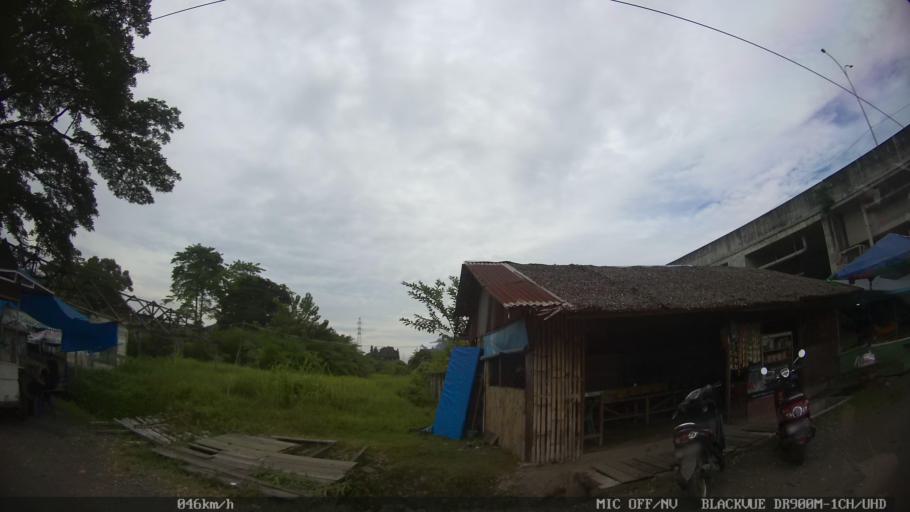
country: ID
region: North Sumatra
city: Sunggal
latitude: 3.6362
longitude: 98.5924
